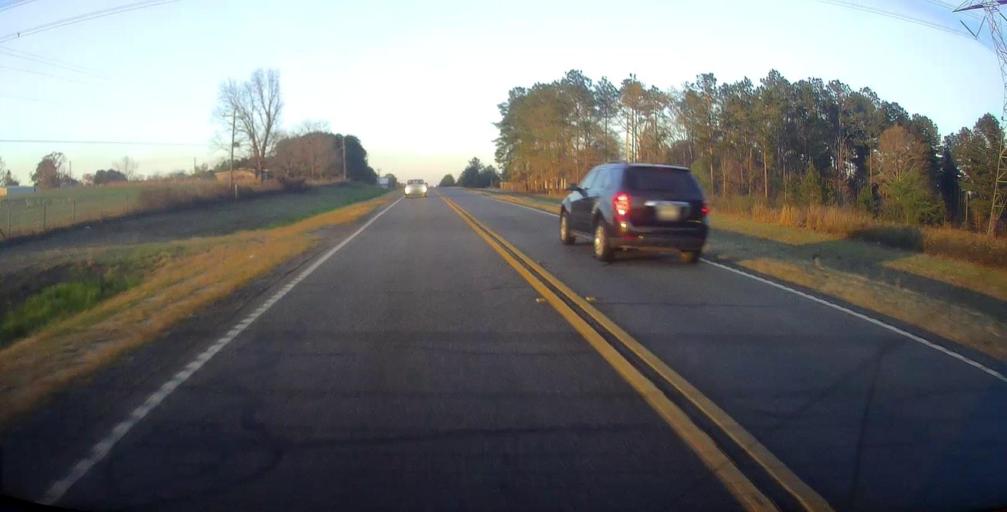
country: US
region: Georgia
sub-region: Dodge County
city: Eastman
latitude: 32.2485
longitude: -83.1432
